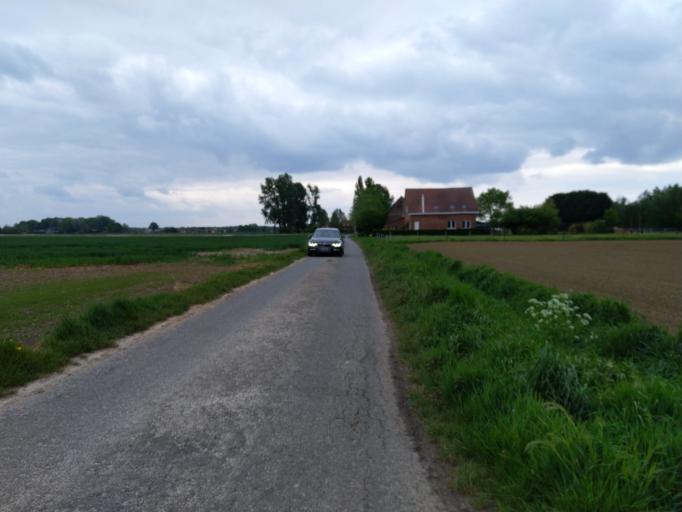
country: BE
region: Wallonia
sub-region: Province du Hainaut
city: Jurbise
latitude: 50.5237
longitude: 3.8846
